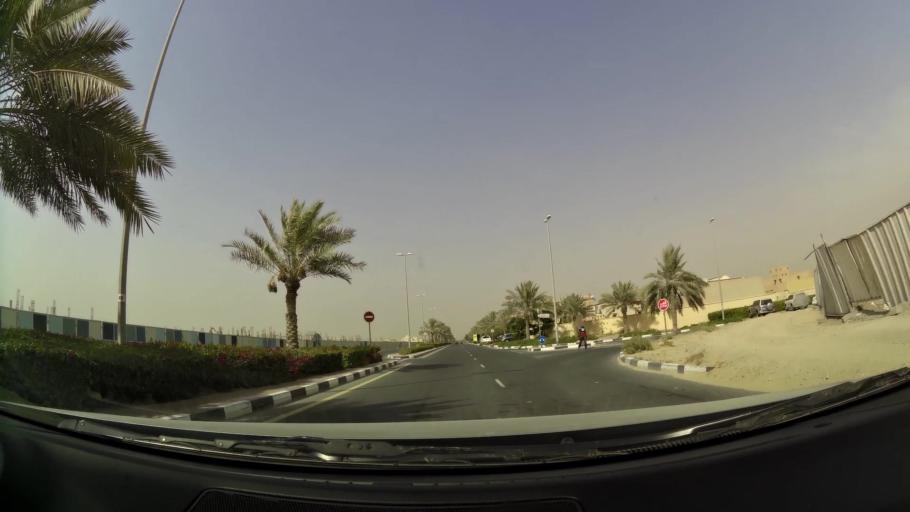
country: AE
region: Ash Shariqah
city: Sharjah
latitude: 25.2632
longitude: 55.4437
